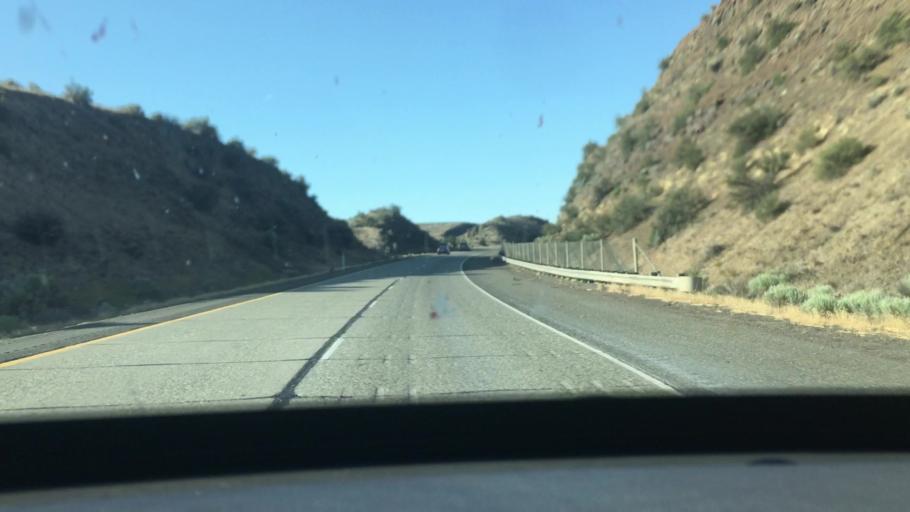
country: US
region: Washington
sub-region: Kittitas County
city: Kittitas
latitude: 46.8019
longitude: -120.3587
